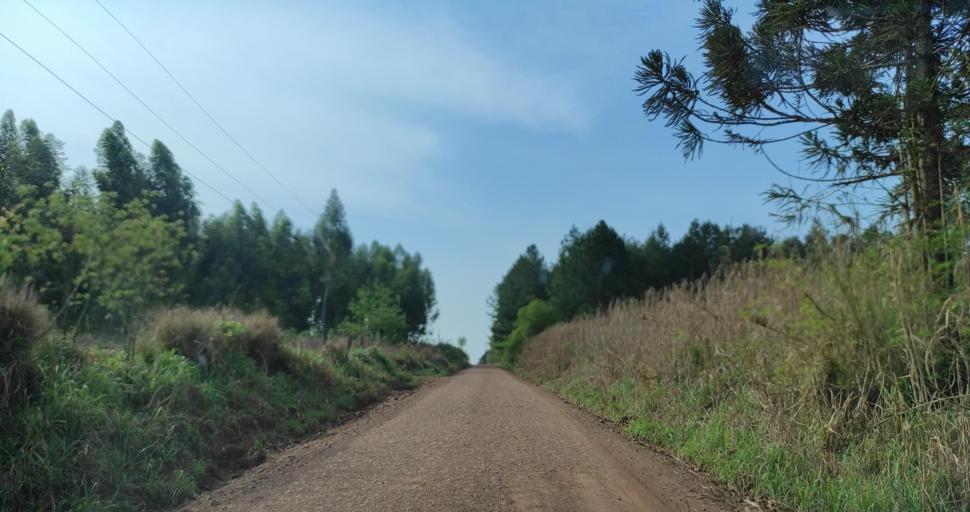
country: AR
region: Misiones
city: Garuhape
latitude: -26.8697
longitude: -55.0054
